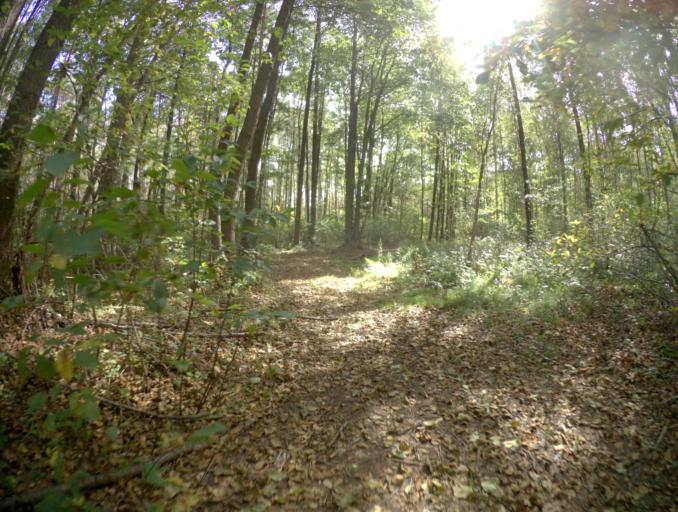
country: RU
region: Vladimir
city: Pokrov
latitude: 55.8457
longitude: 39.1994
